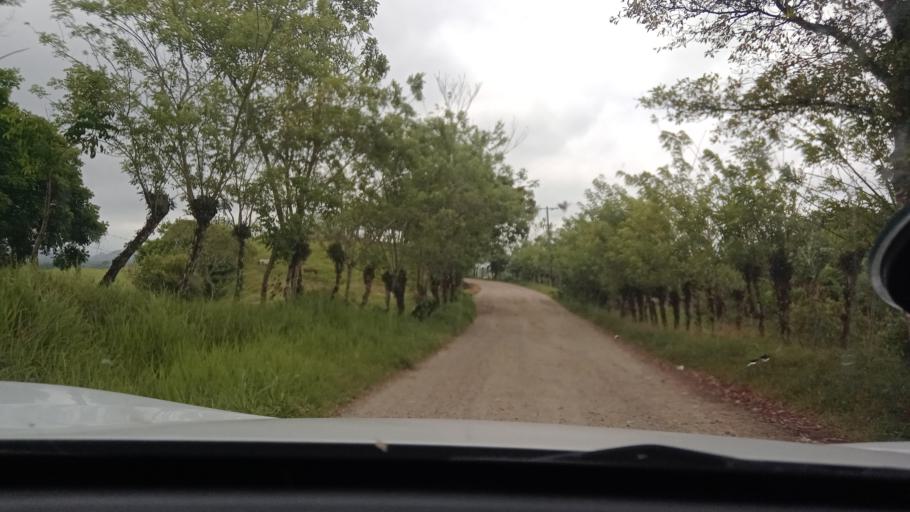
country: MX
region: Tabasco
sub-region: Huimanguillo
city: Francisco Rueda
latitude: 17.5654
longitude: -94.0253
